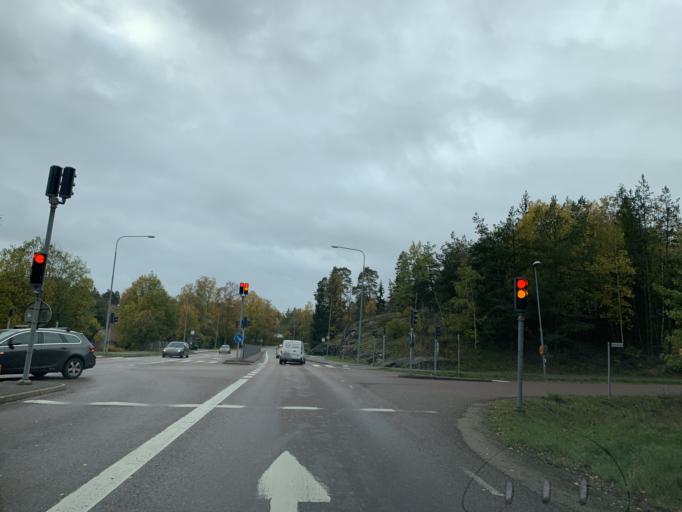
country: SE
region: Stockholm
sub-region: Botkyrka Kommun
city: Tumba
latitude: 59.1833
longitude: 17.8152
